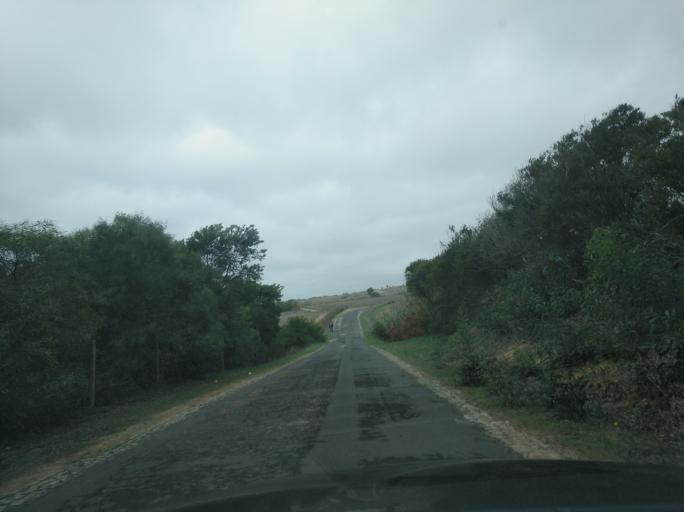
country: PT
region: Setubal
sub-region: Sines
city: Porto Covo
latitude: 37.8366
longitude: -8.7873
